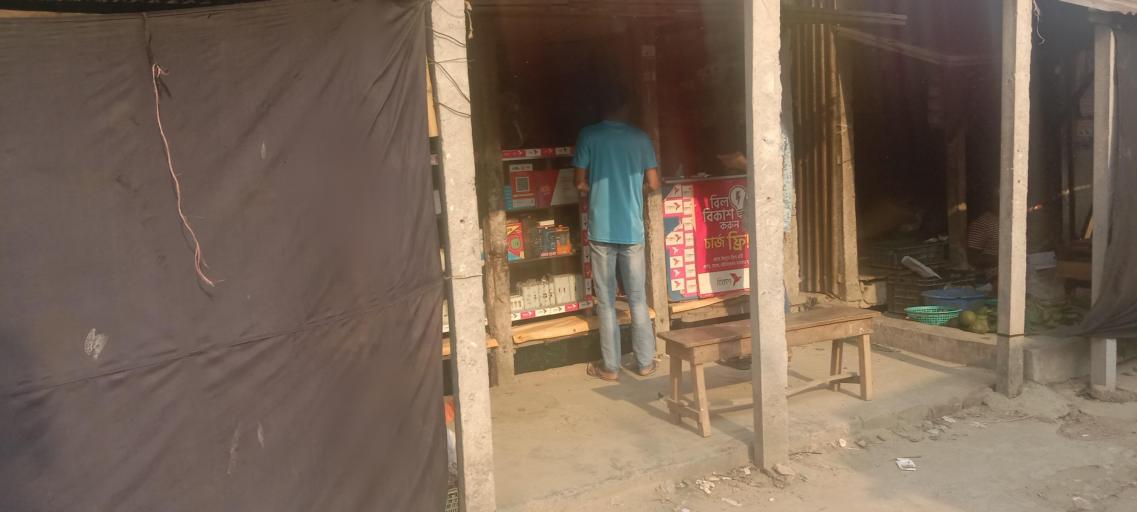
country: BD
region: Dhaka
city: Narayanganj
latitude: 23.6458
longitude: 90.4552
